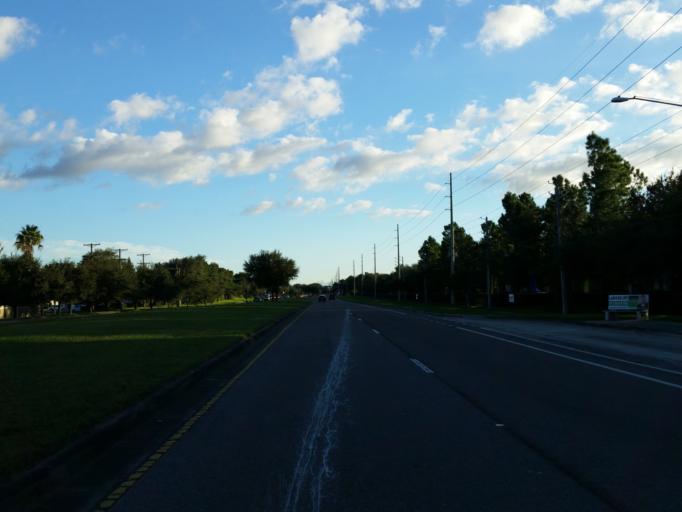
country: US
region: Florida
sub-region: Hillsborough County
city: Brandon
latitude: 27.9162
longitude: -82.3188
